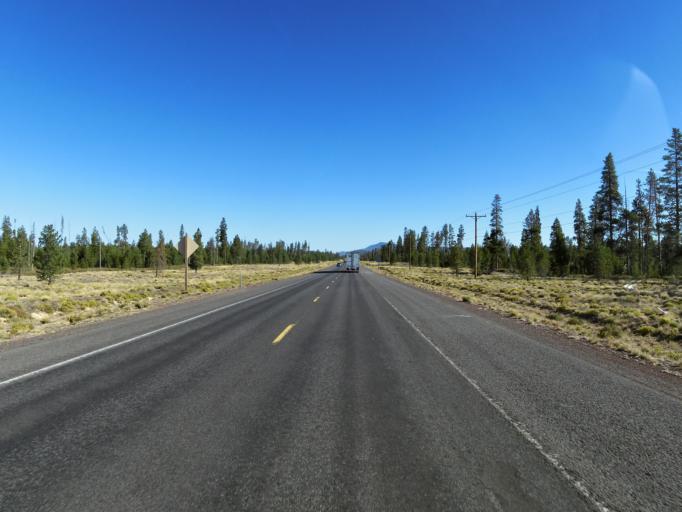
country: US
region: Oregon
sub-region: Deschutes County
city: La Pine
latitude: 43.1554
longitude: -121.7941
